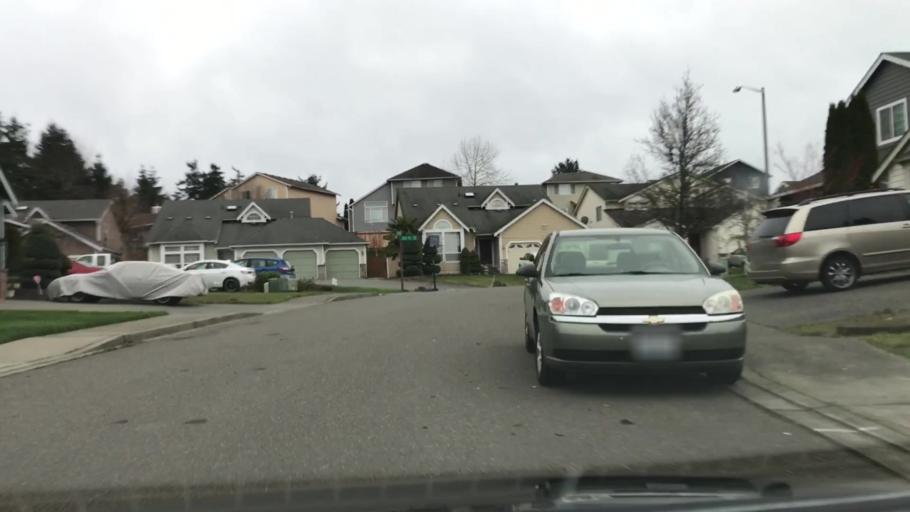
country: US
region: Washington
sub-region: King County
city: Kent
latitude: 47.3850
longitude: -122.2068
